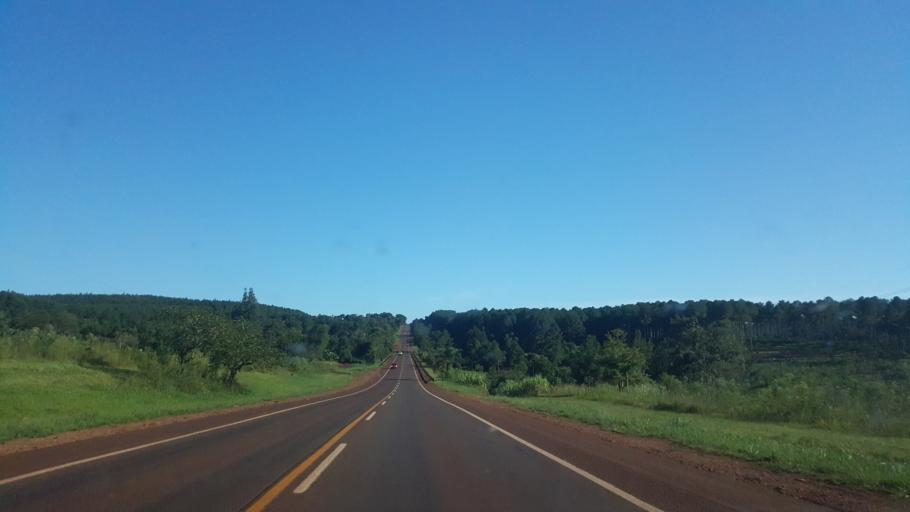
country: AR
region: Misiones
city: Puerto Esperanza
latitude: -26.1482
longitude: -54.5827
